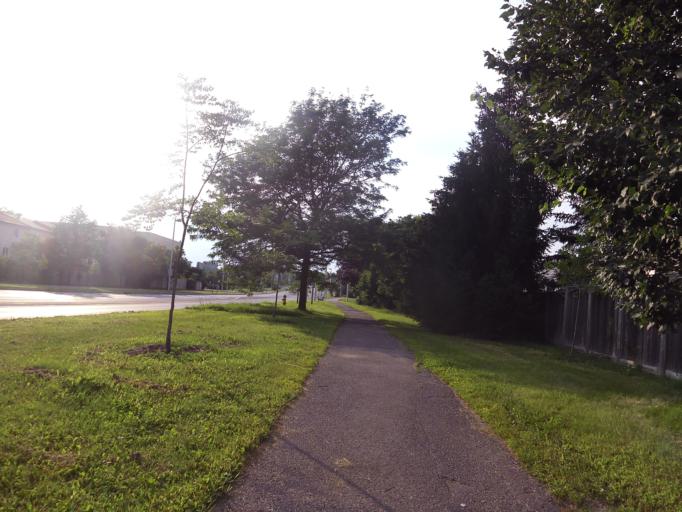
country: CA
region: Ontario
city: Bells Corners
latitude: 45.3094
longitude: -75.8991
